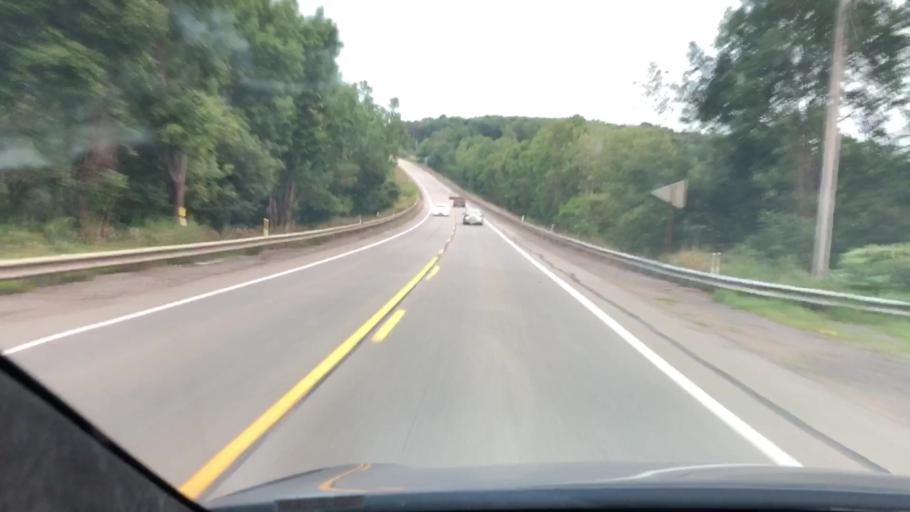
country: US
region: Pennsylvania
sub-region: Butler County
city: Shanor-Northvue
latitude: 40.9159
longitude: -79.9422
